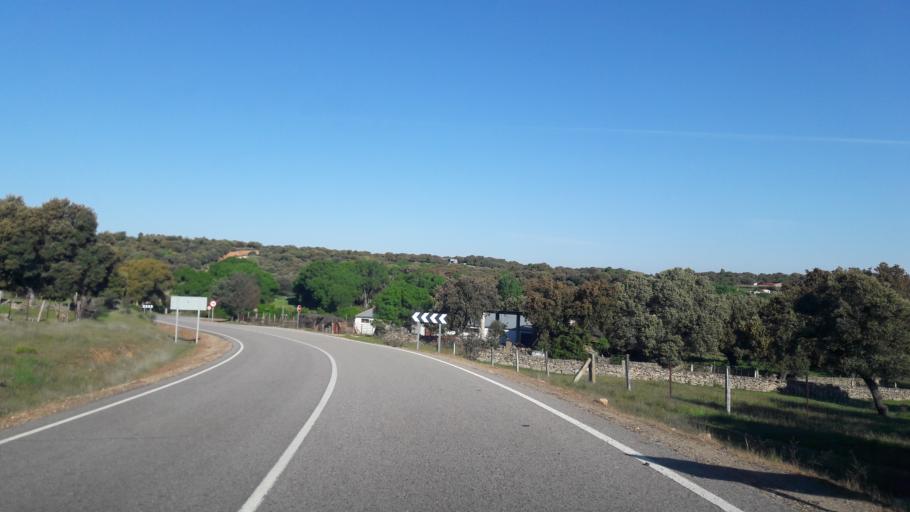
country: ES
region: Castille and Leon
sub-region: Provincia de Salamanca
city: Bogajo
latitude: 40.9032
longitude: -6.5282
